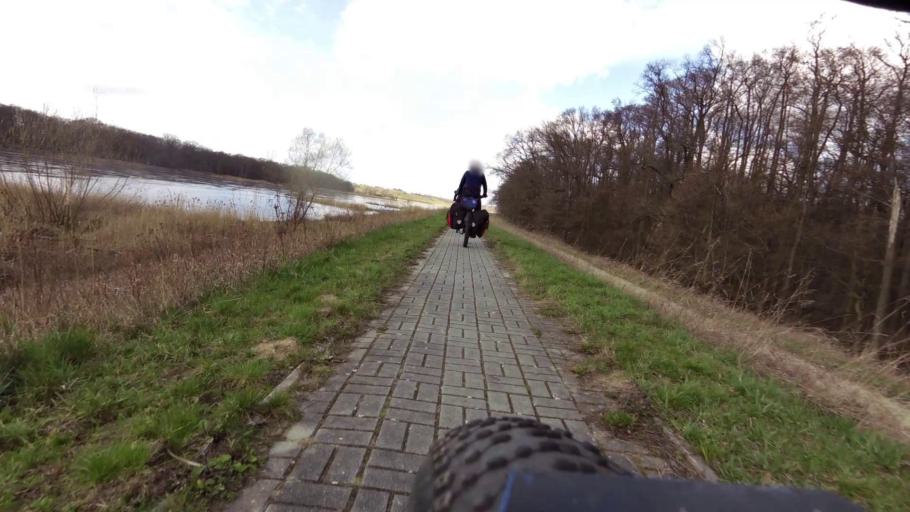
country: PL
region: Lubusz
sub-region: Powiat slubicki
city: Slubice
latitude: 52.3863
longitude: 14.5446
